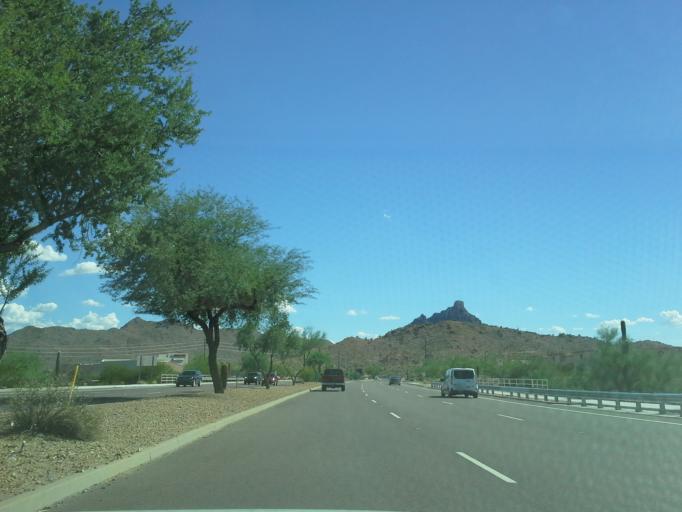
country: US
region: Arizona
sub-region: Maricopa County
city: Fountain Hills
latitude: 33.5708
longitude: -111.7118
